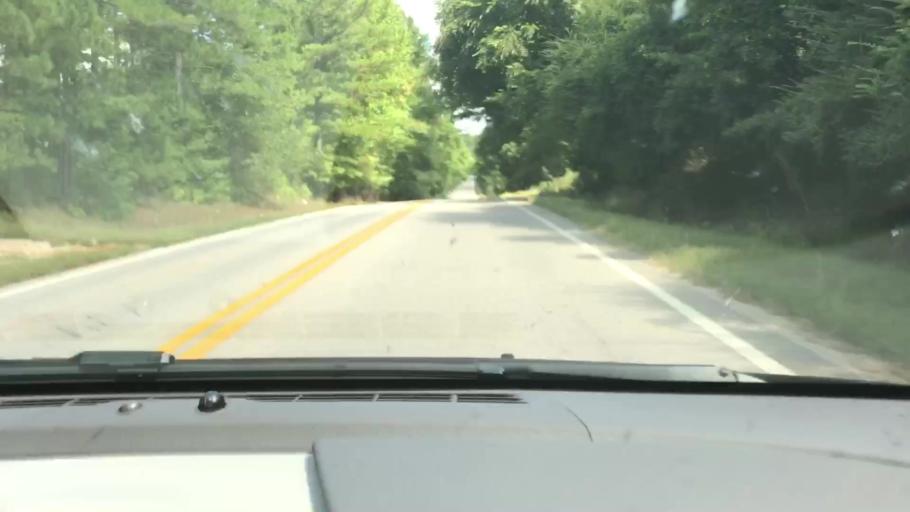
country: US
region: Georgia
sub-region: Troup County
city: La Grange
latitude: 32.9237
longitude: -85.0201
